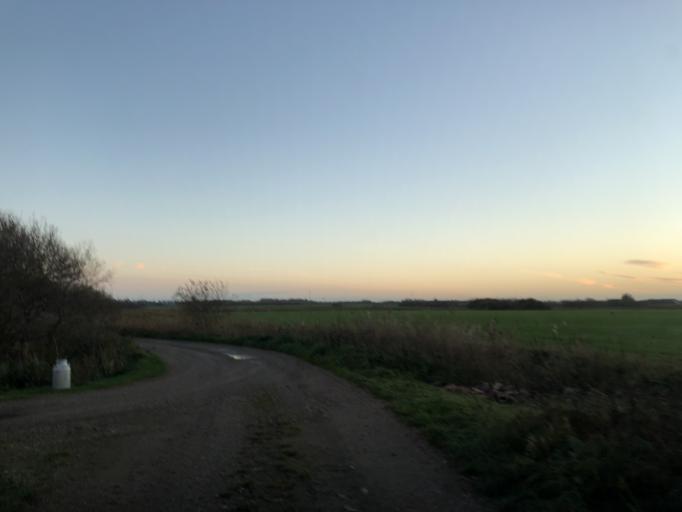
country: DK
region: Central Jutland
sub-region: Holstebro Kommune
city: Ulfborg
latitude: 56.2897
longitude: 8.2920
